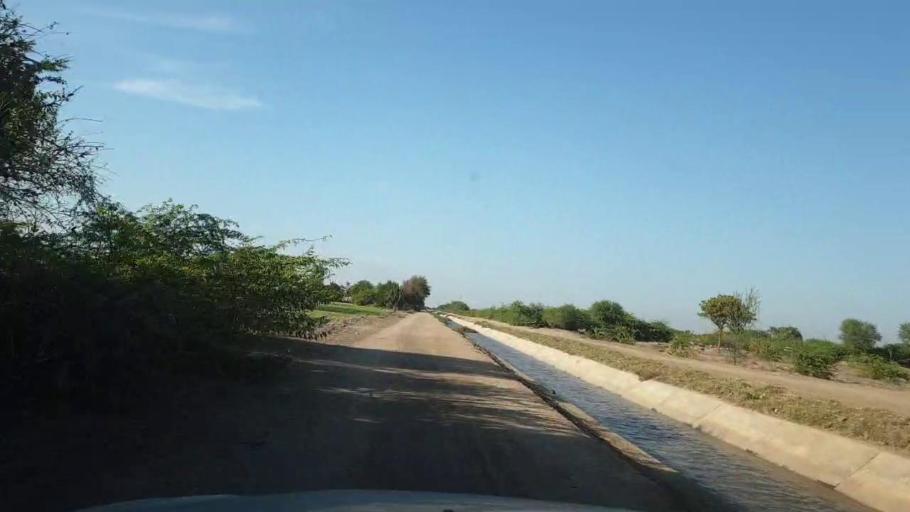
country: PK
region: Sindh
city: Kunri
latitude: 25.0928
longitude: 69.4286
